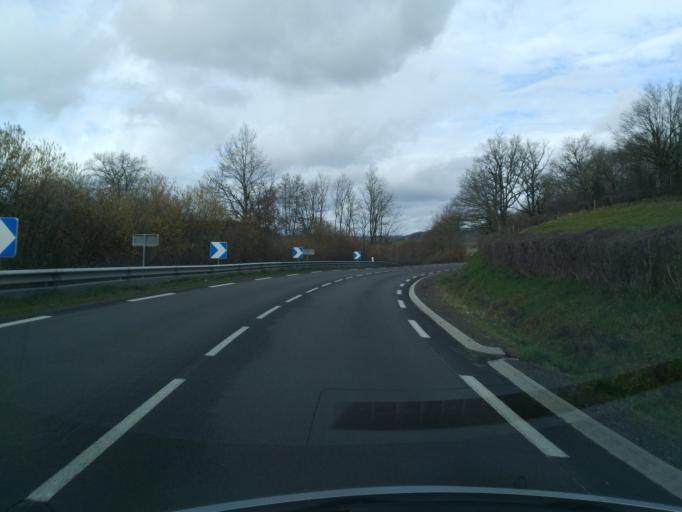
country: FR
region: Bourgogne
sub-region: Departement de Saone-et-Loire
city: Montcenis
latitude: 46.8036
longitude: 4.3779
